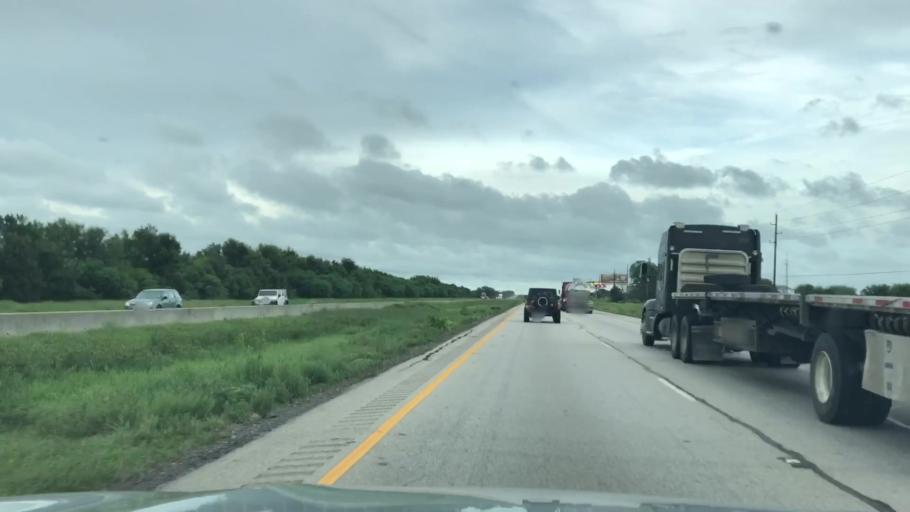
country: US
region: Texas
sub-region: Austin County
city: Sealy
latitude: 29.7756
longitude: -96.0928
